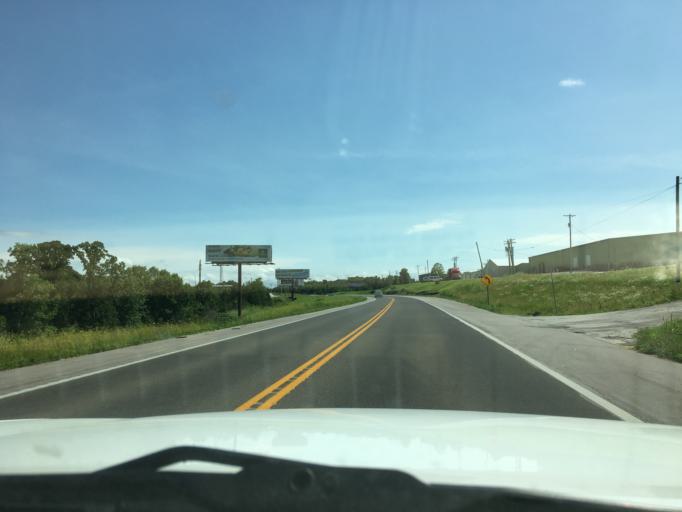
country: US
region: Missouri
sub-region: Franklin County
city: Union
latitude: 38.4925
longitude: -91.0045
